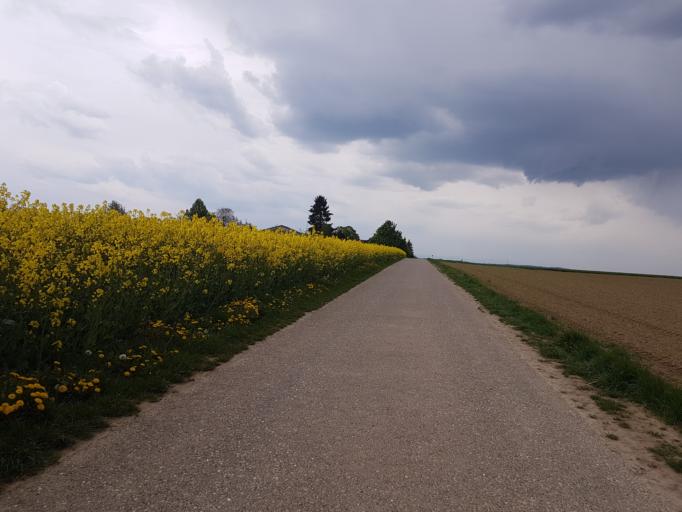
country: DE
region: Baden-Wuerttemberg
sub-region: Regierungsbezirk Stuttgart
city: Bondorf
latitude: 48.5145
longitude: 8.8084
